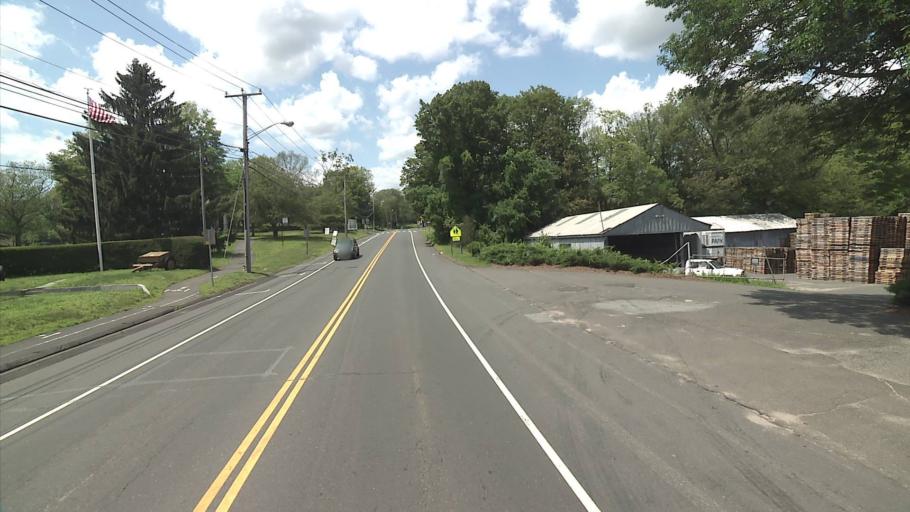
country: US
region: Connecticut
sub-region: Middlesex County
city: Higganum
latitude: 41.4969
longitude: -72.5594
